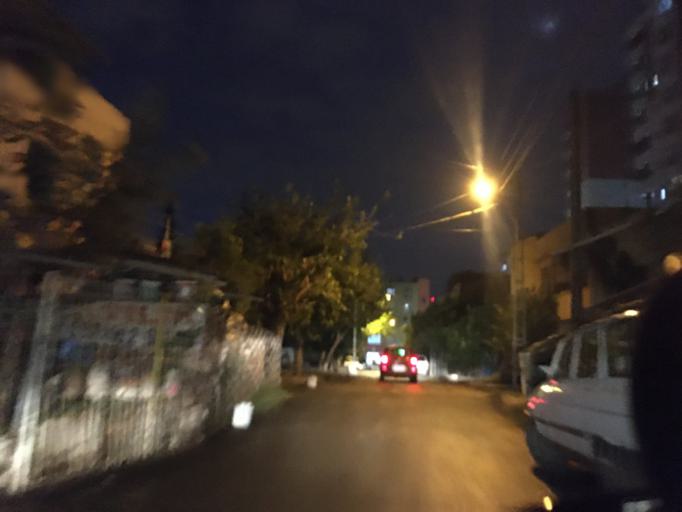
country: TR
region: Adana
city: Seyhan
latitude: 37.0253
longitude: 35.2833
